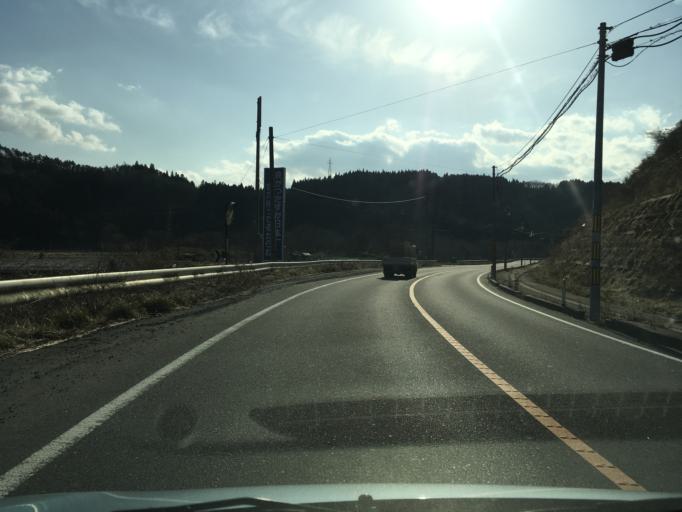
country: JP
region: Iwate
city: Ichinoseki
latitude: 38.7765
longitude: 141.3470
